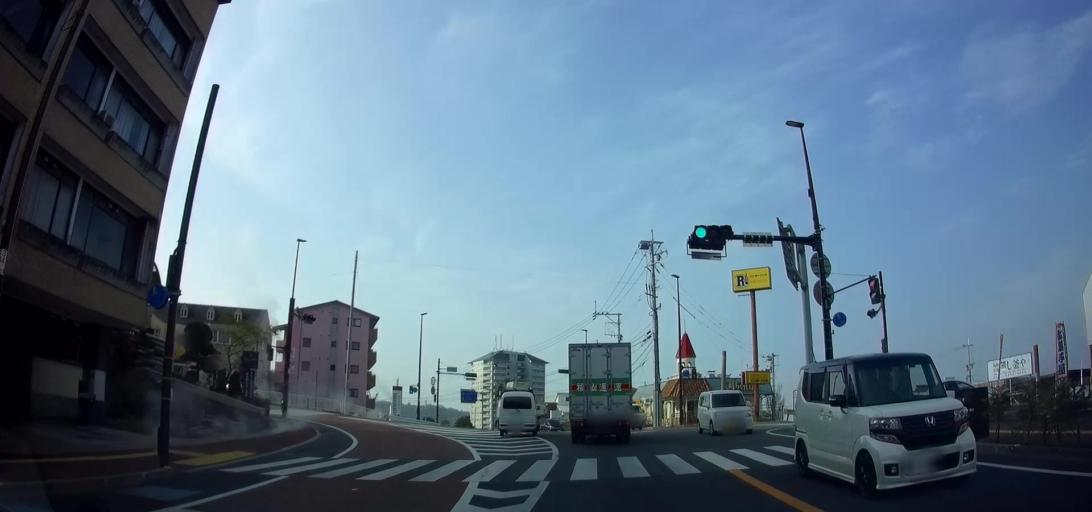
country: JP
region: Nagasaki
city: Shimabara
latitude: 32.7258
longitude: 130.2050
